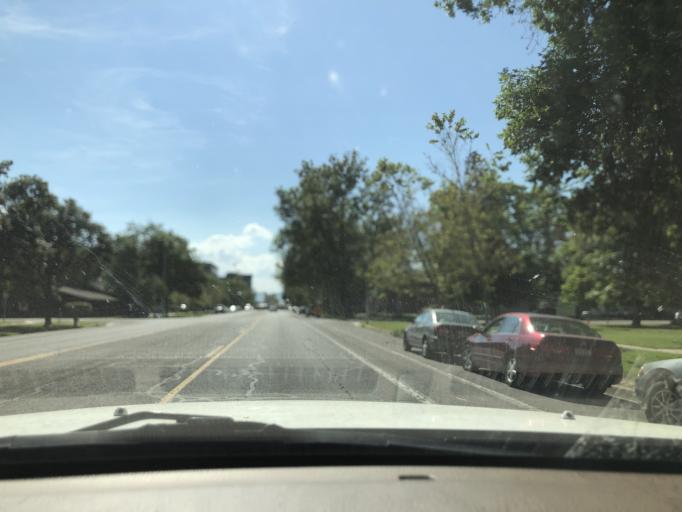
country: US
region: Utah
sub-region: Utah County
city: Provo
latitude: 40.2337
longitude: -111.6527
